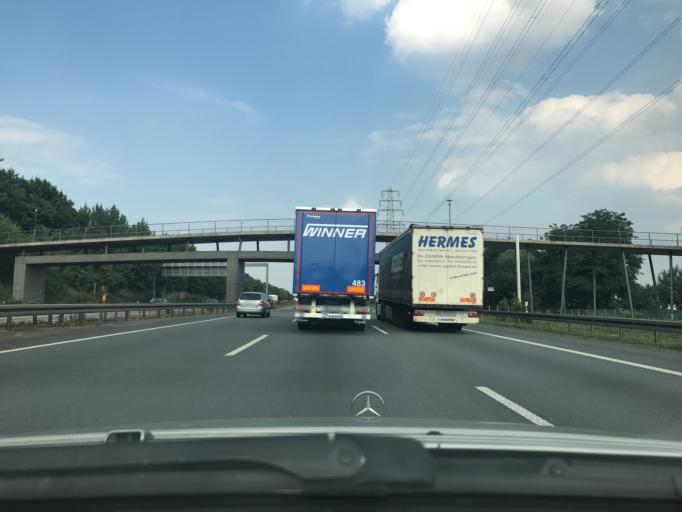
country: DE
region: North Rhine-Westphalia
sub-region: Regierungsbezirk Dusseldorf
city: Oberhausen
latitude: 51.4962
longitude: 6.8772
